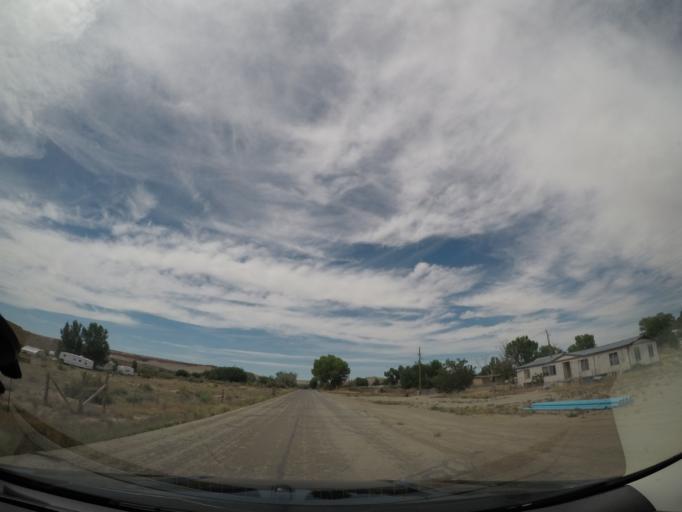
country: US
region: Utah
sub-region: Emery County
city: Ferron
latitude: 38.3694
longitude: -110.7168
